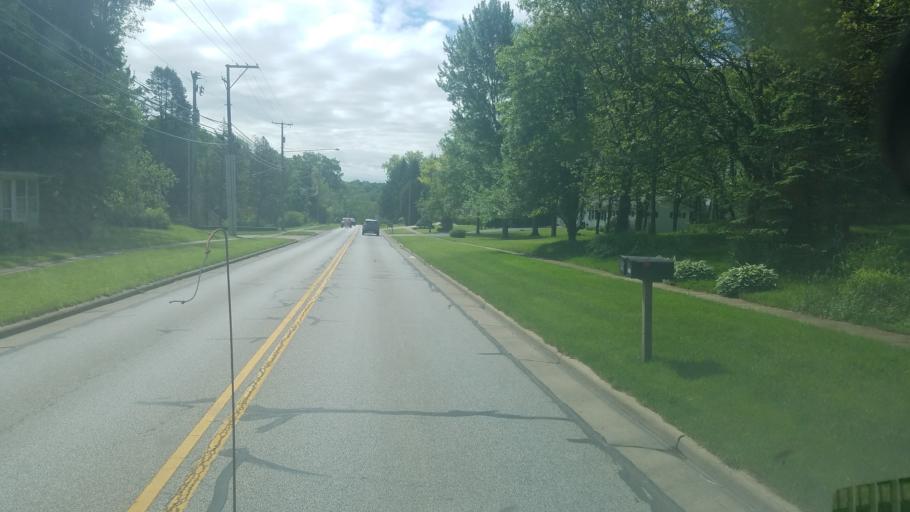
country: US
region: Ohio
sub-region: Wayne County
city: Wooster
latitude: 40.8429
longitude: -81.9339
